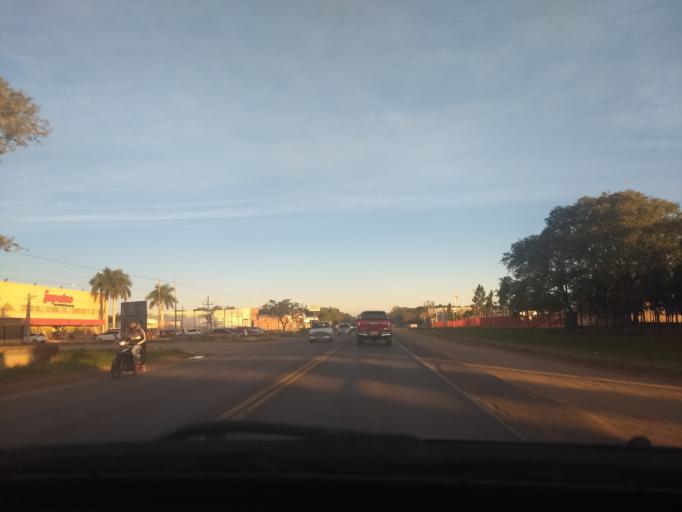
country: AR
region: Corrientes
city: Corrientes
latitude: -27.4916
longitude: -58.7792
